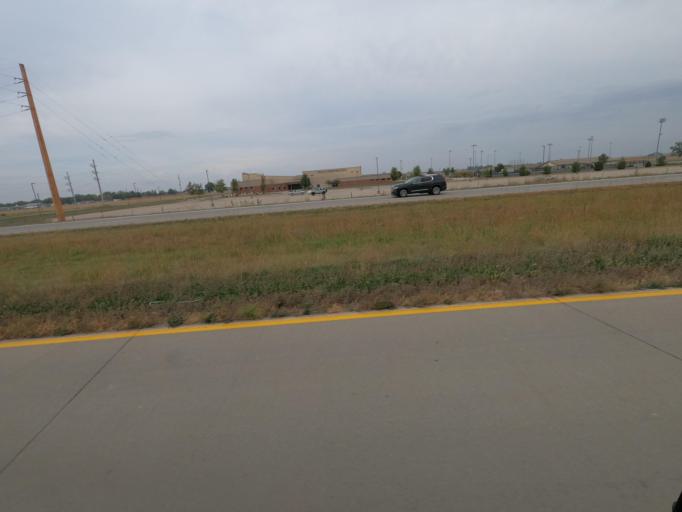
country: US
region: Iowa
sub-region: Marion County
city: Pella
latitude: 41.3903
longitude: -92.8890
